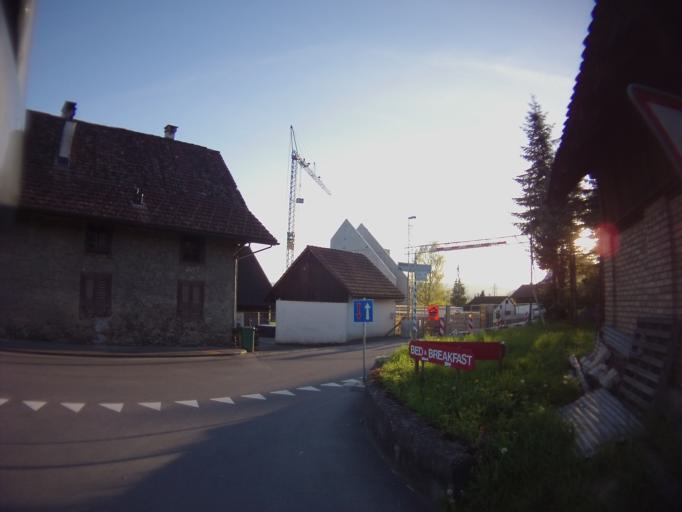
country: CH
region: Zurich
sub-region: Bezirk Affoltern
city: Obfelden / Toussen
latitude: 47.2589
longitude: 8.4406
